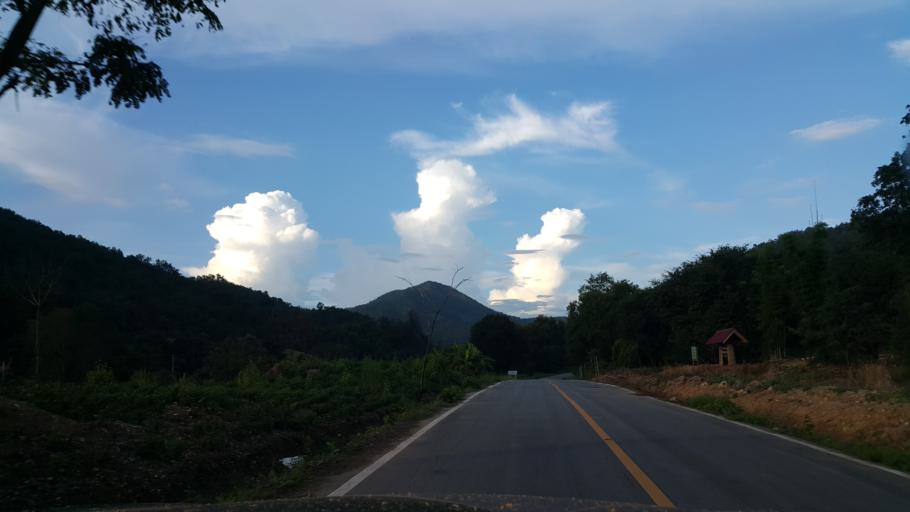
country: TH
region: Mae Hong Son
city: Mae Hi
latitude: 19.2329
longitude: 98.4447
